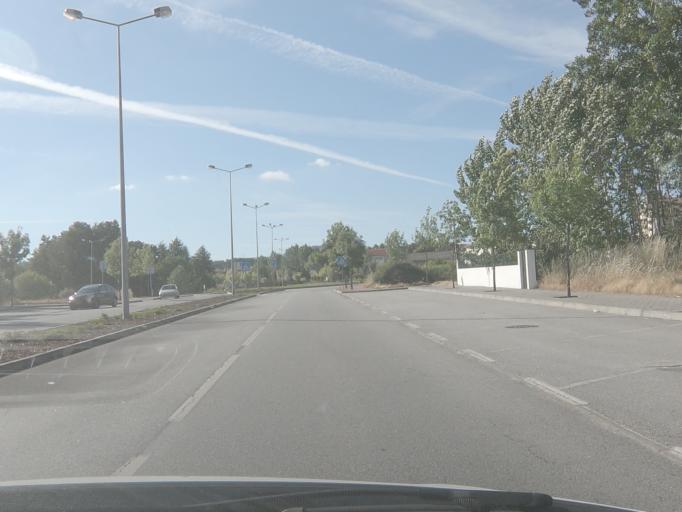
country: PT
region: Viseu
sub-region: Viseu
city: Viseu
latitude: 40.6711
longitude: -7.9048
